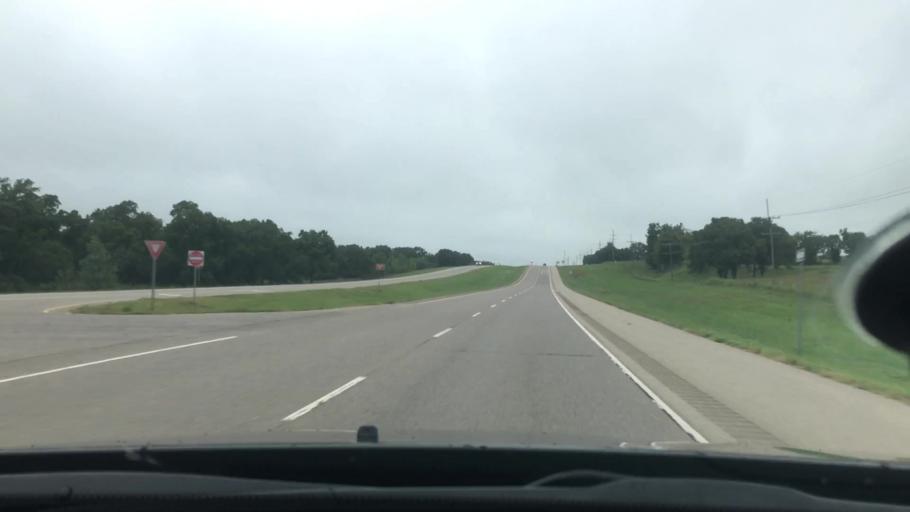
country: US
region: Oklahoma
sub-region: Seminole County
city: Seminole
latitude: 35.3405
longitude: -96.6715
